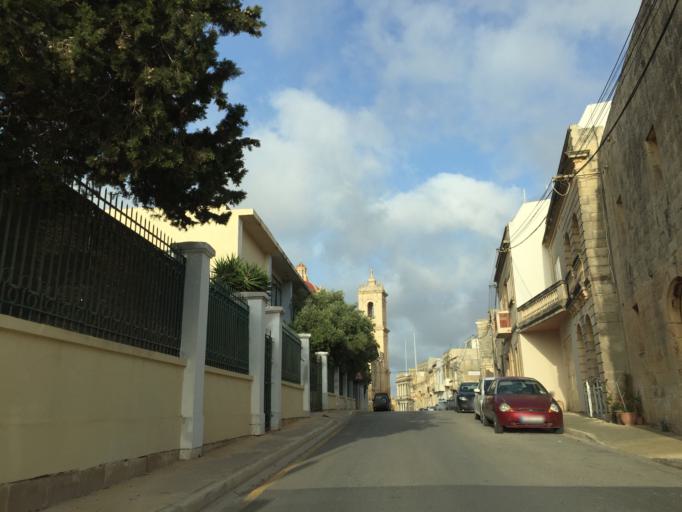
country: MT
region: Il-Qrendi
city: Qrendi
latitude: 35.8344
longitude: 14.4560
